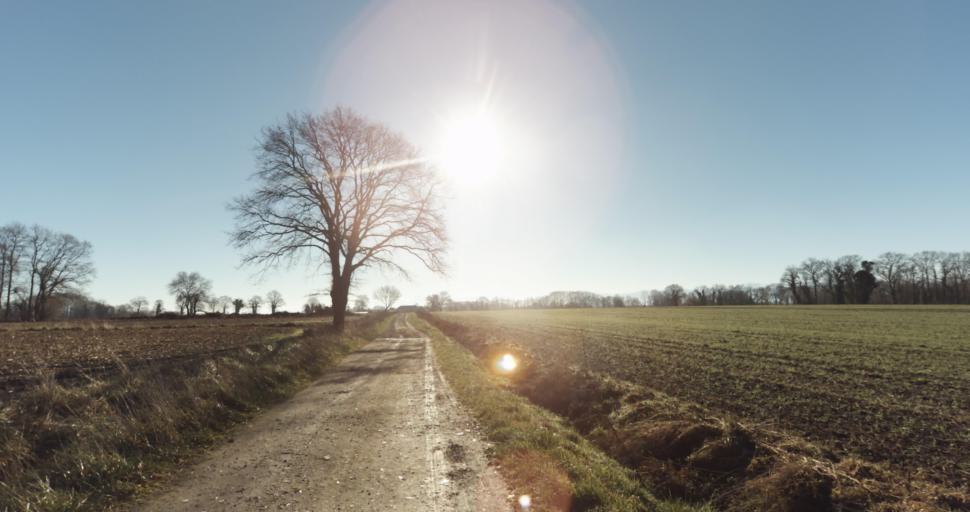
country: FR
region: Aquitaine
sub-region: Departement des Pyrenees-Atlantiques
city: Morlaas
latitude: 43.3451
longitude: -0.2398
